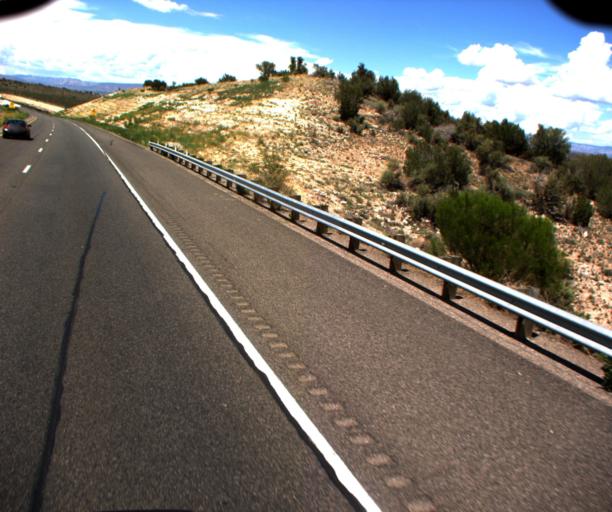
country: US
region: Arizona
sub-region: Yavapai County
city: Verde Village
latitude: 34.6736
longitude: -111.9696
